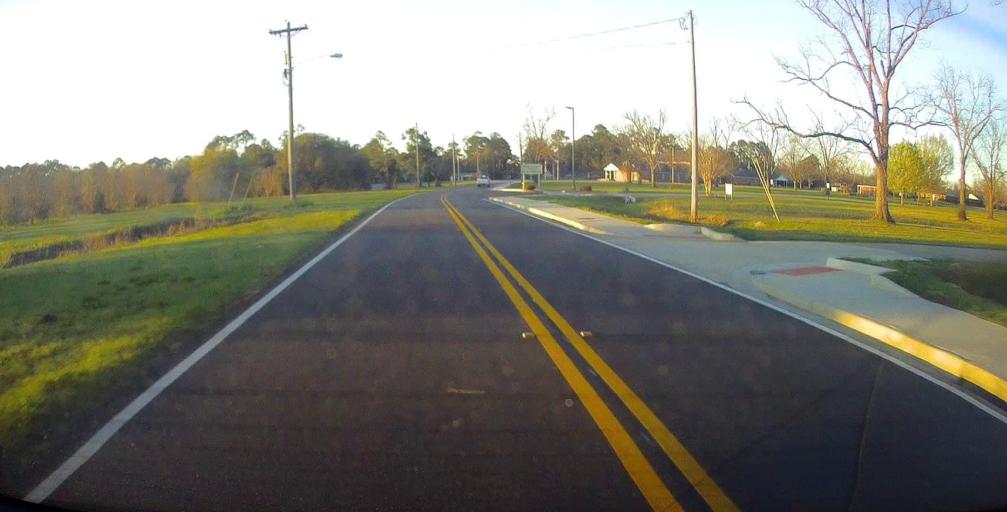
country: US
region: Georgia
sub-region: Crisp County
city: Cordele
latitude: 31.9704
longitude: -83.7648
